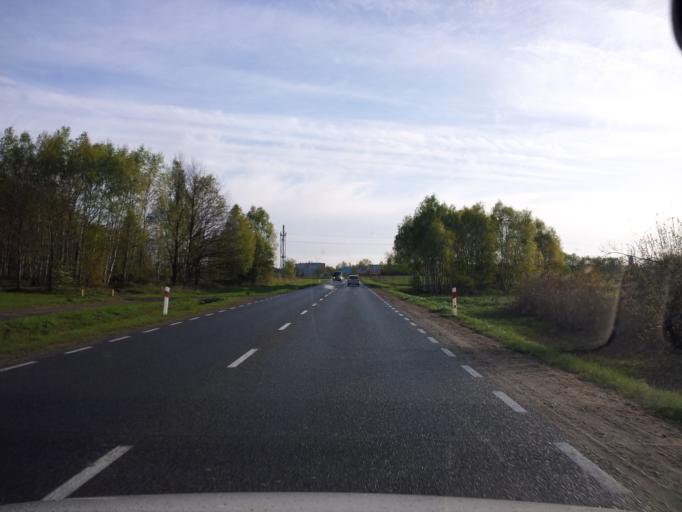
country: PL
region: Lubusz
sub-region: Powiat zarski
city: Zary
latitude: 51.6233
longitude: 15.1129
